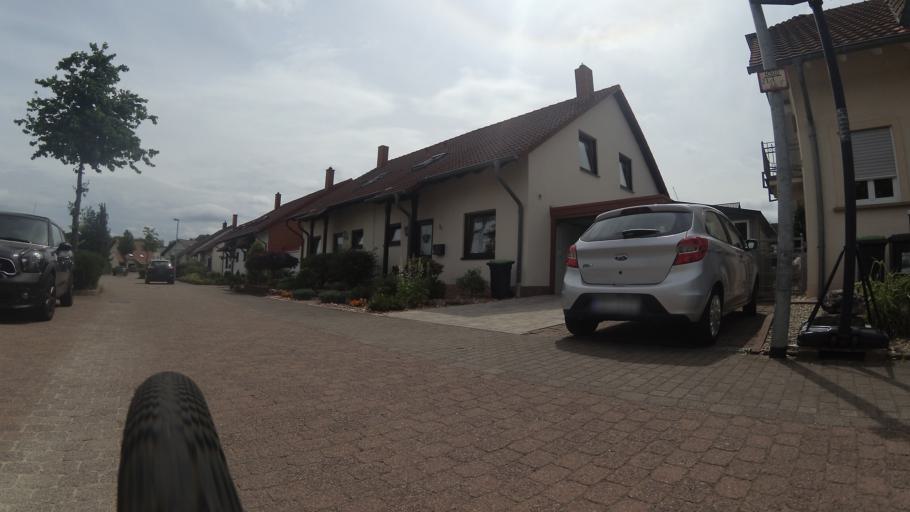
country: DE
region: Saarland
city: Sankt Ingbert
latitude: 49.2779
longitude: 7.1671
